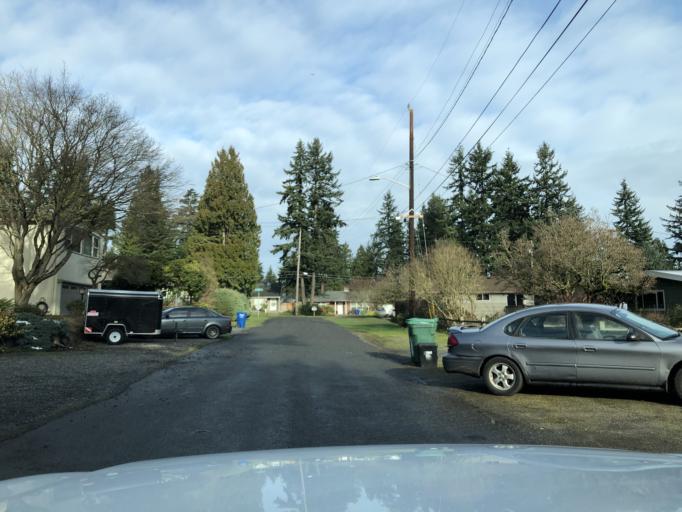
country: US
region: Washington
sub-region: King County
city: Lake Forest Park
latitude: 47.7240
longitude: -122.3005
